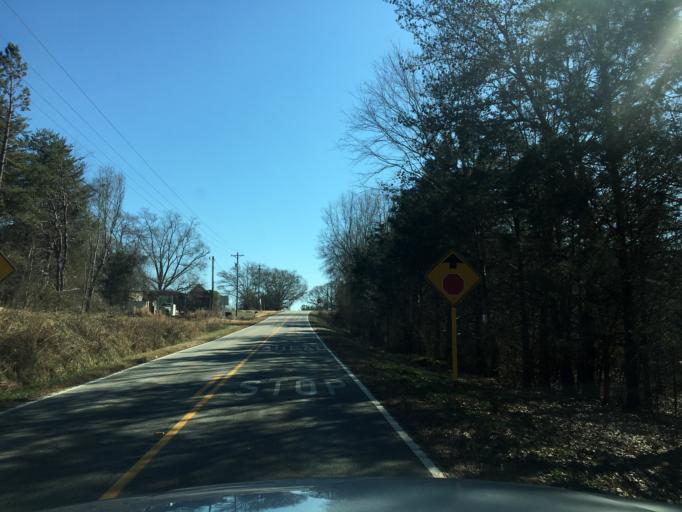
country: US
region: South Carolina
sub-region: Pickens County
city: Liberty
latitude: 34.7991
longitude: -82.7407
